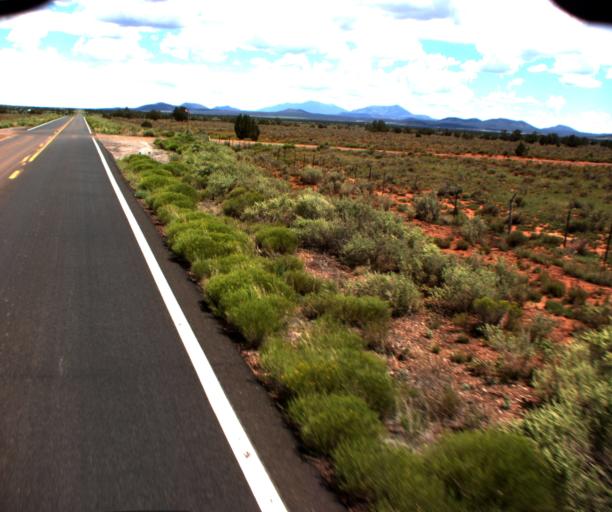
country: US
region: Arizona
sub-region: Coconino County
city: Williams
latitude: 35.6192
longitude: -112.0965
